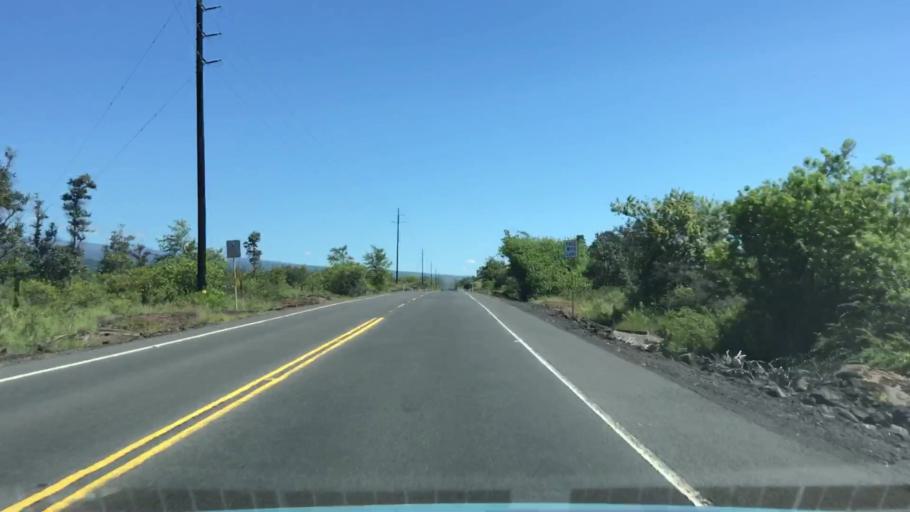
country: US
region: Hawaii
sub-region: Hawaii County
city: Pahala
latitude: 19.2383
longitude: -155.4485
